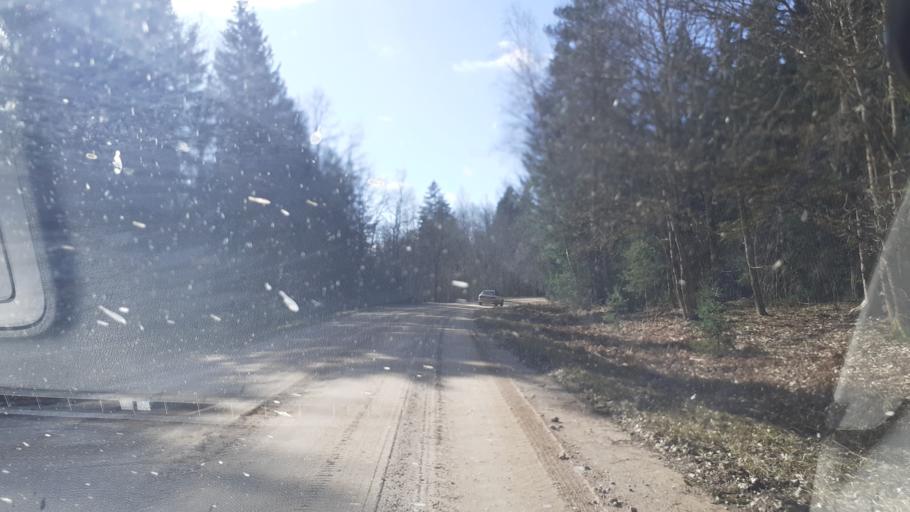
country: LV
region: Kuldigas Rajons
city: Kuldiga
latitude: 56.9108
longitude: 22.0823
